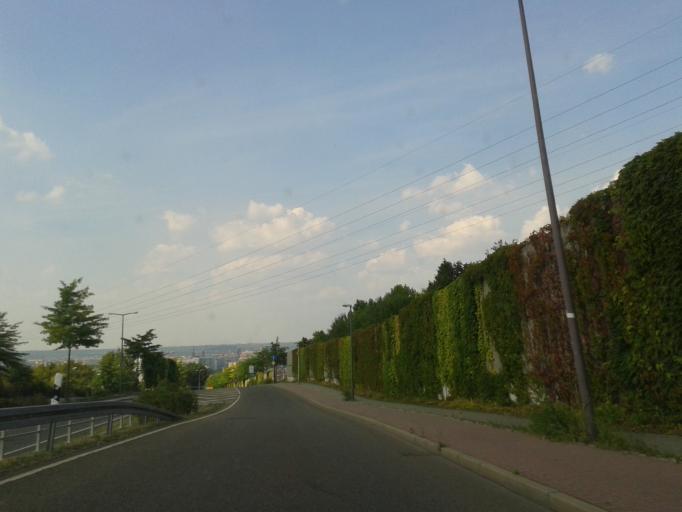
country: DE
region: Saxony
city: Dresden
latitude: 51.0210
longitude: 13.7301
